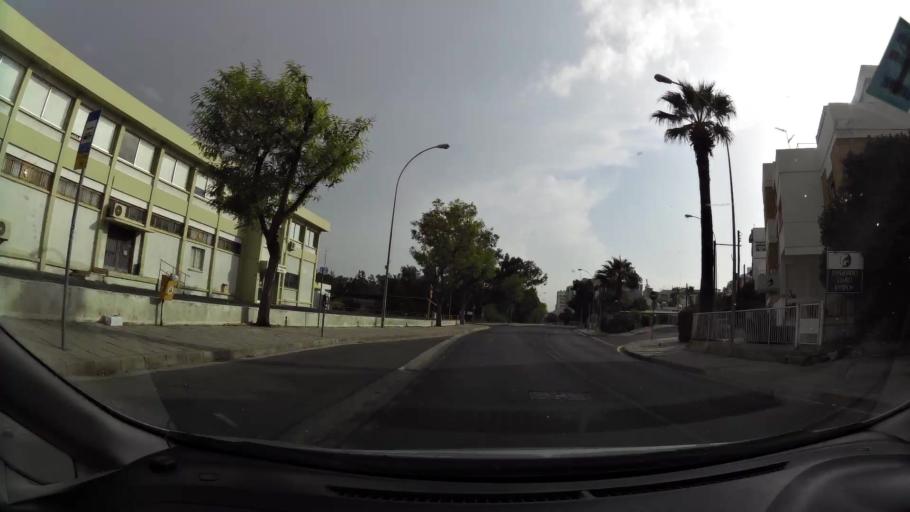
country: CY
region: Lefkosia
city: Nicosia
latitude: 35.1606
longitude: 33.3462
